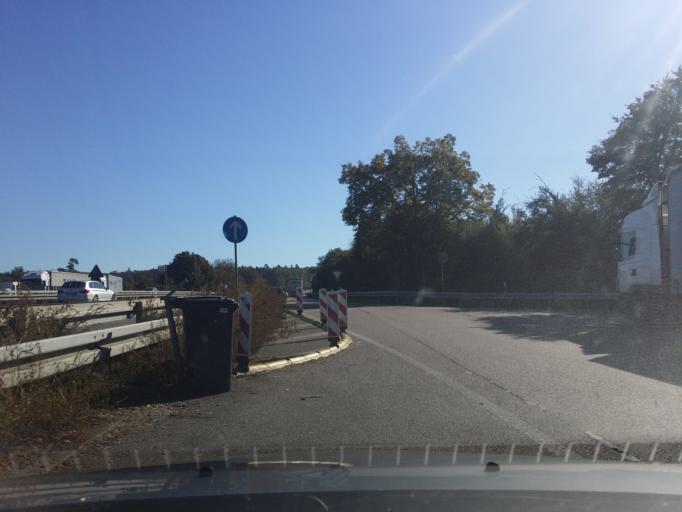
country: DE
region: Baden-Wuerttemberg
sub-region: Karlsruhe Region
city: Niefern-Oschelbronn
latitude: 48.9067
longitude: 8.7736
